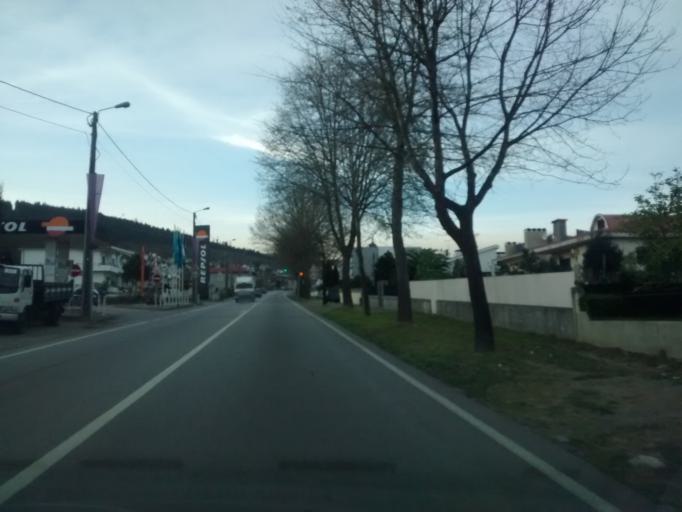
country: PT
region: Braga
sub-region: Guimaraes
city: Brito
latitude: 41.4937
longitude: -8.3617
